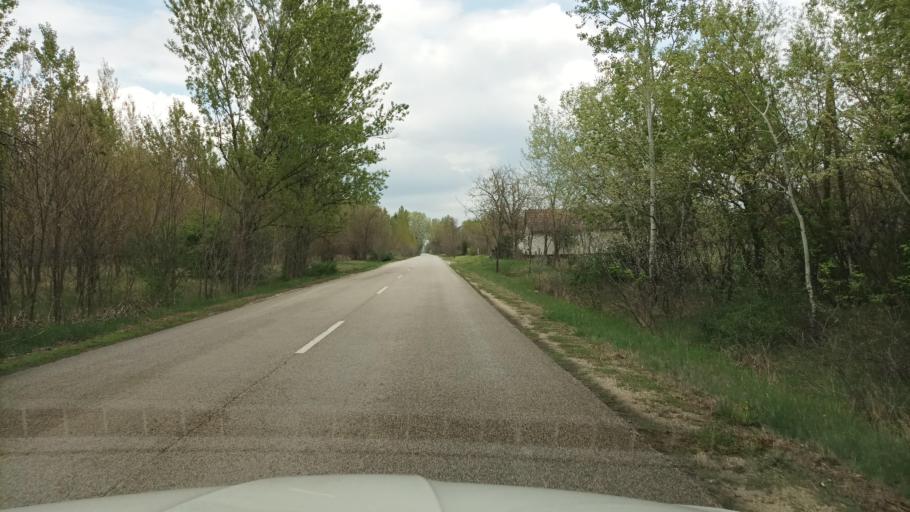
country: HU
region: Pest
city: Kocser
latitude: 47.0220
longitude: 19.9341
